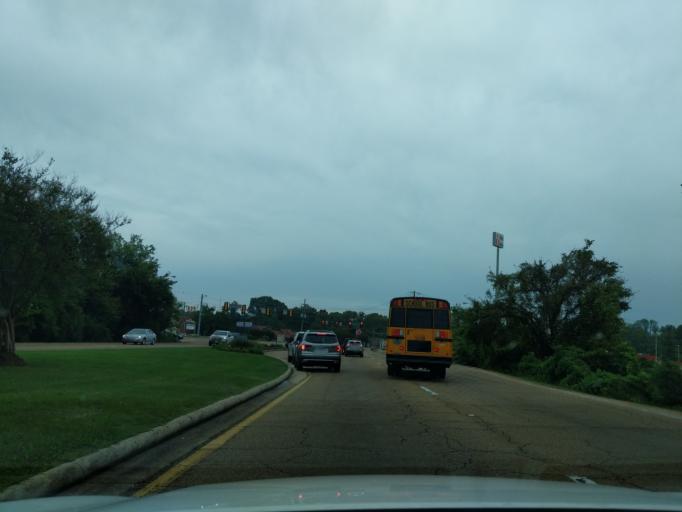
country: US
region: Mississippi
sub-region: Warren County
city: Vicksburg
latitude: 32.3161
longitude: -90.8769
